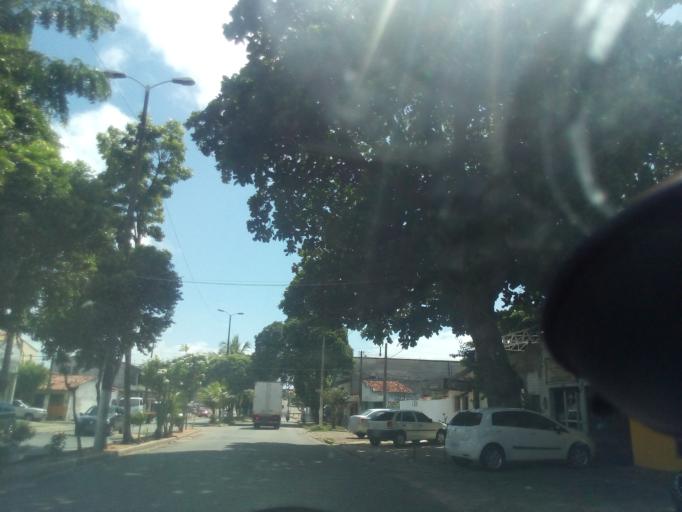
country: BR
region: Rio Grande do Norte
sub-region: Natal
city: Natal
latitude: -5.8229
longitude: -35.2334
